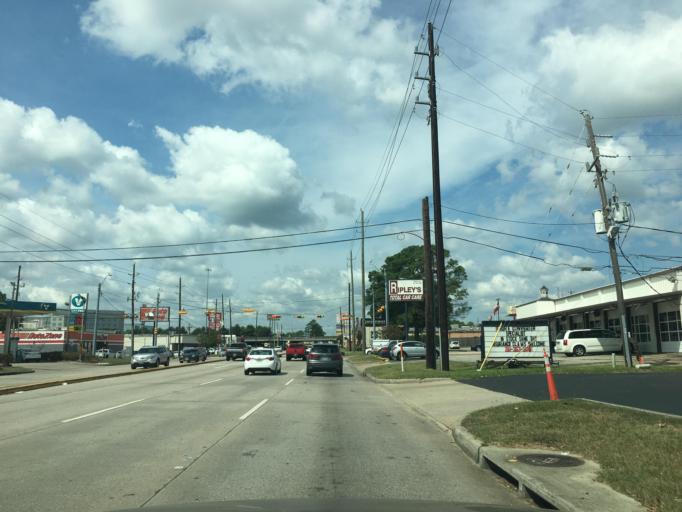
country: US
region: Texas
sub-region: Montgomery County
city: Oak Ridge North
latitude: 30.1271
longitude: -95.4392
